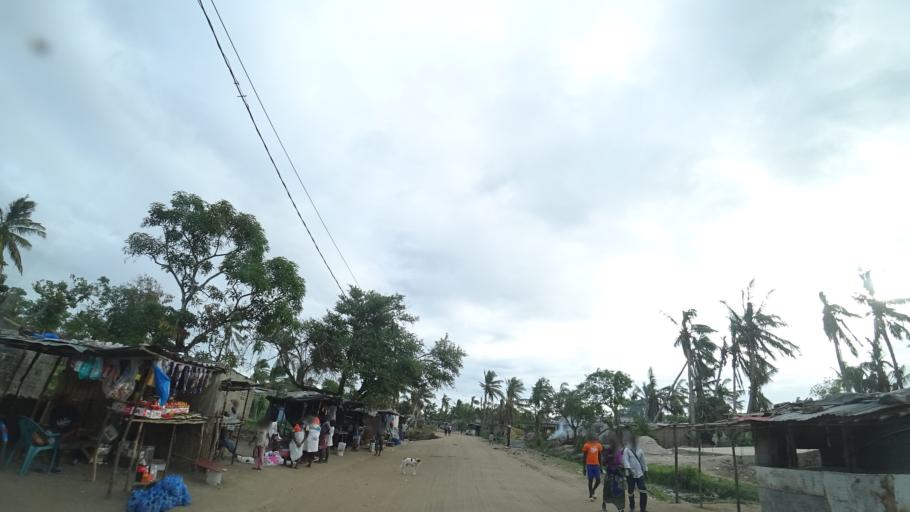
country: MZ
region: Sofala
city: Beira
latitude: -19.7708
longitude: 34.8879
